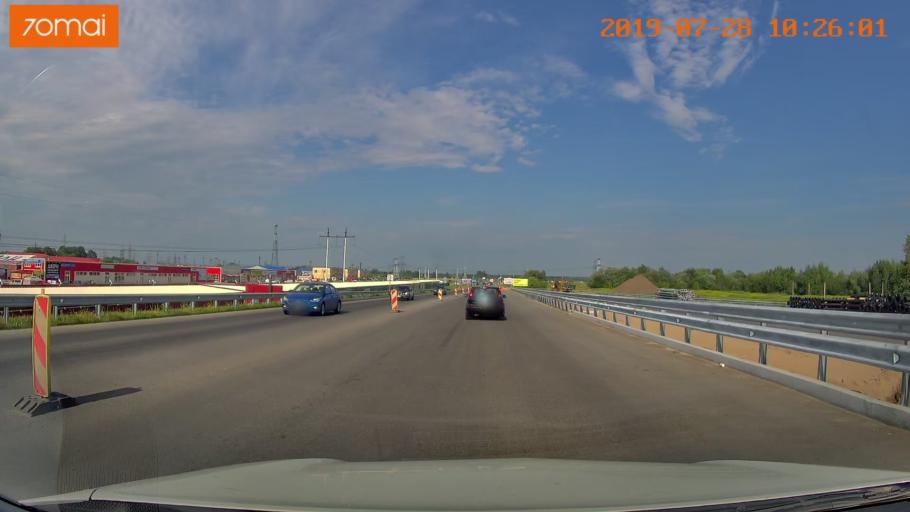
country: RU
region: Kaliningrad
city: Maloye Isakovo
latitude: 54.7682
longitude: 20.5333
